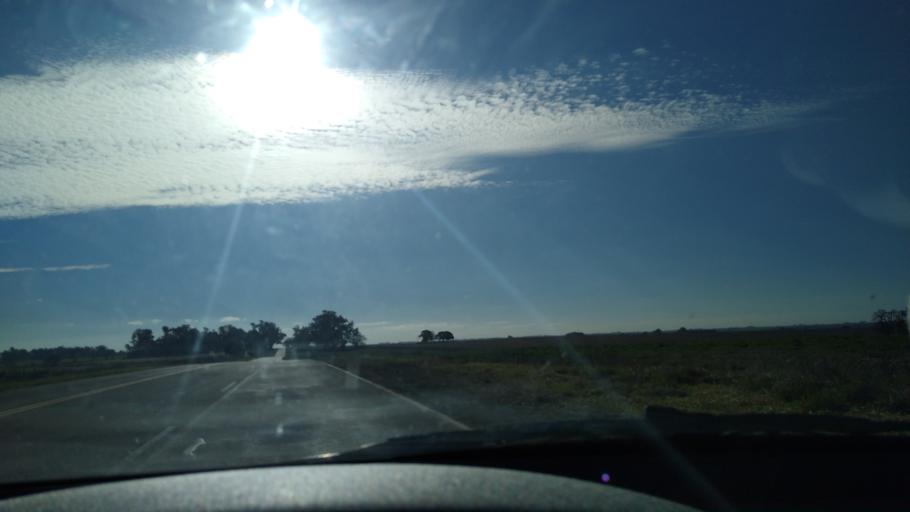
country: AR
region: Entre Rios
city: Aranguren
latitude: -32.3352
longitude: -60.3817
